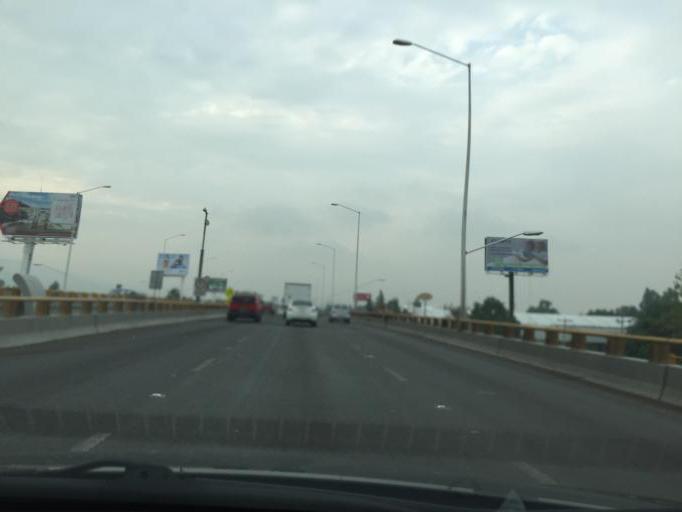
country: MX
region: Guanajuato
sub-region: Leon
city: Medina
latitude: 21.1715
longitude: -101.6580
